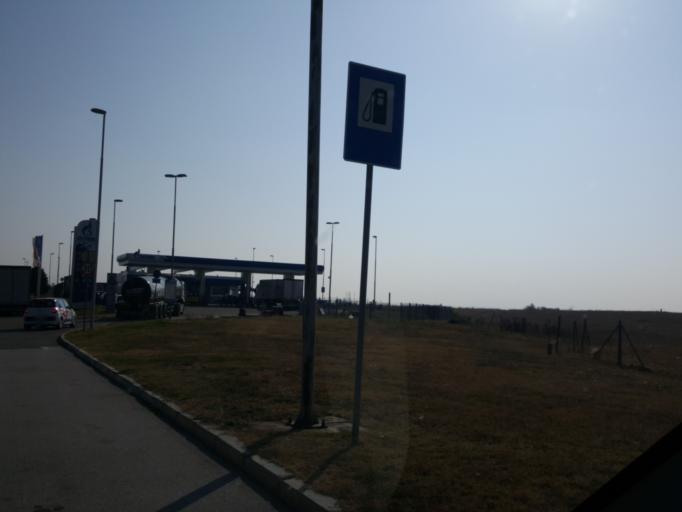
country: RS
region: Central Serbia
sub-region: Nisavski Okrug
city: Nis
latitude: 43.3809
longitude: 21.8088
